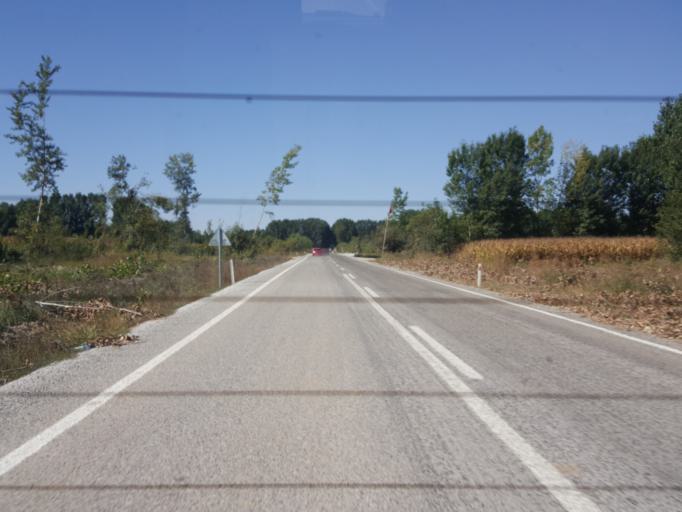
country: TR
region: Tokat
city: Pazar
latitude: 40.2679
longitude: 36.2019
